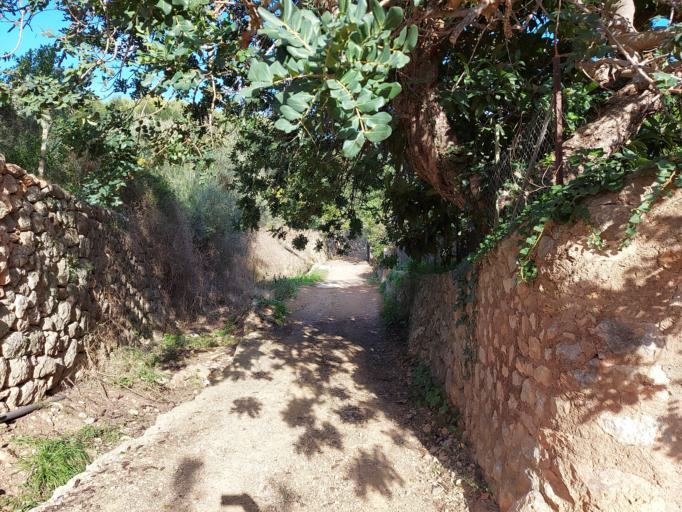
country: ES
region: Balearic Islands
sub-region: Illes Balears
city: Soller
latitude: 39.7770
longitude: 2.7260
